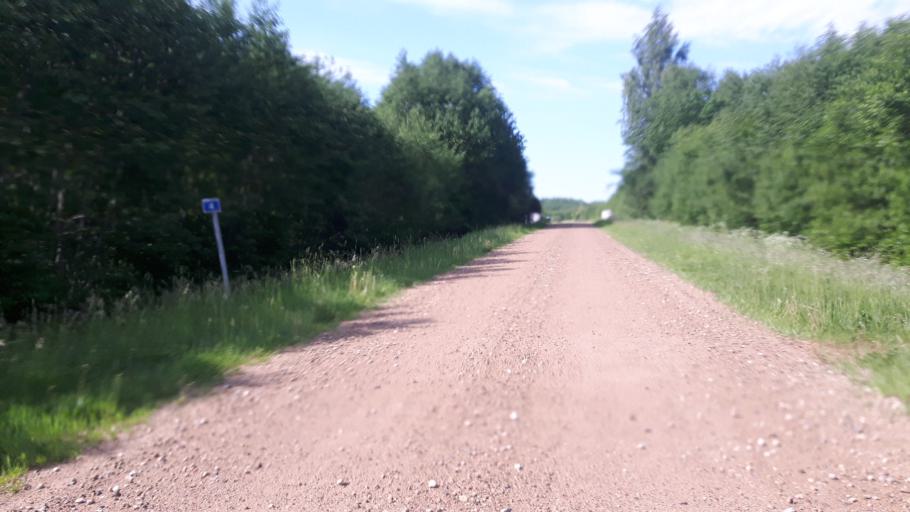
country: EE
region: Paernumaa
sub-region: Vaendra vald (alev)
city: Vandra
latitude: 58.7051
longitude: 25.0319
